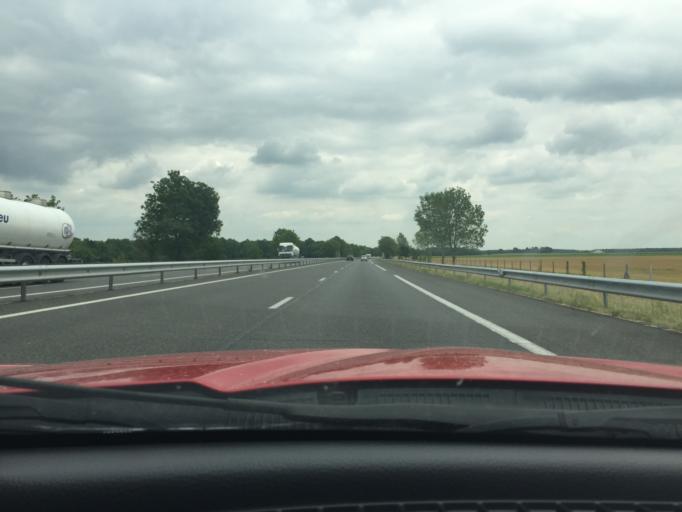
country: FR
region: Picardie
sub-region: Departement de l'Aisne
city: Saint-Erme-Outre-et-Ramecourt
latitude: 49.5568
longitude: 3.8165
